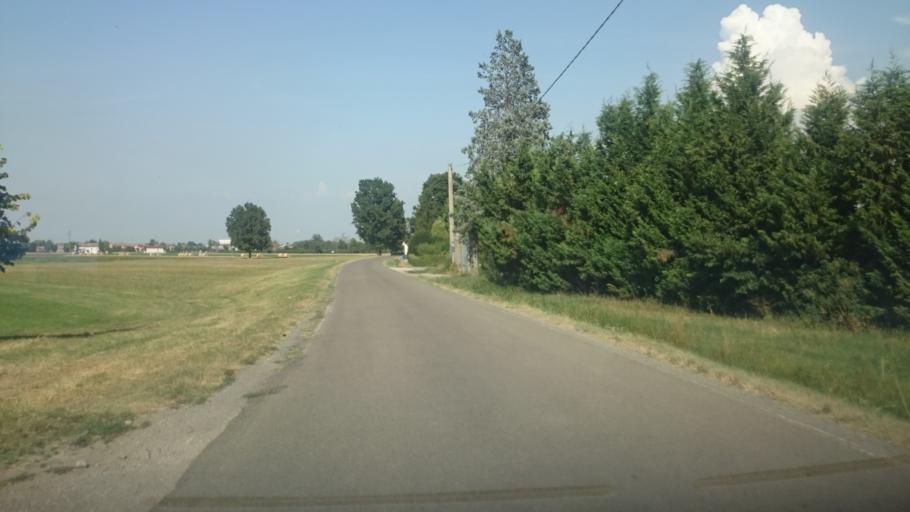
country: IT
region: Emilia-Romagna
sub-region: Provincia di Reggio Emilia
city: Bagno
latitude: 44.6466
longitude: 10.7508
